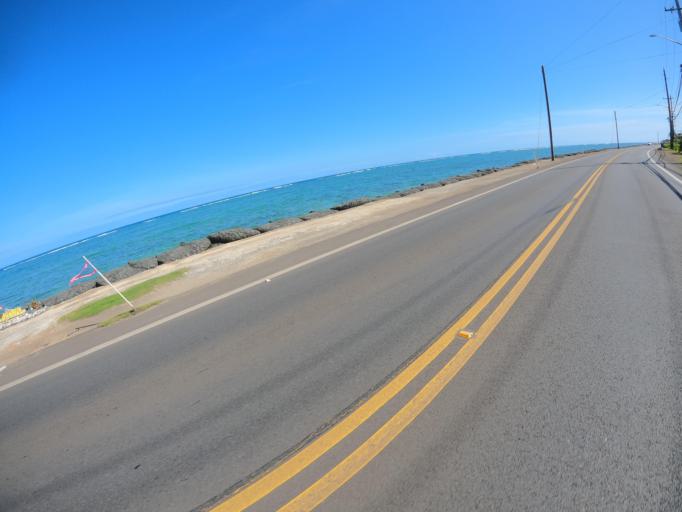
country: US
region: Hawaii
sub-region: Honolulu County
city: Hau'ula
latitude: 21.6053
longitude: -157.9018
